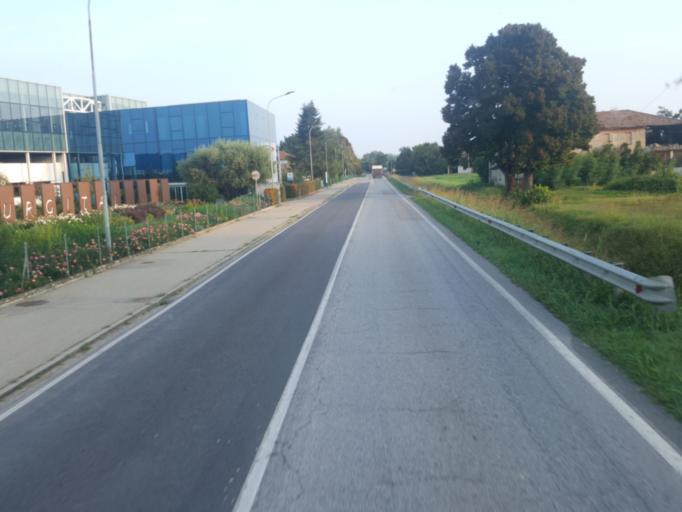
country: IT
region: Emilia-Romagna
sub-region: Provincia di Ravenna
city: Lavezzola
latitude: 44.5693
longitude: 11.8759
